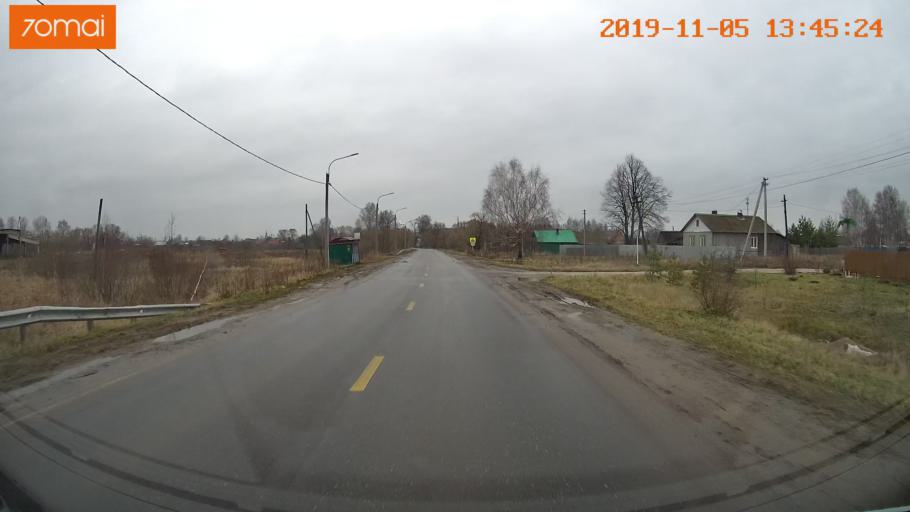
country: RU
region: Ivanovo
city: Shuya
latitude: 56.9883
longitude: 41.4125
